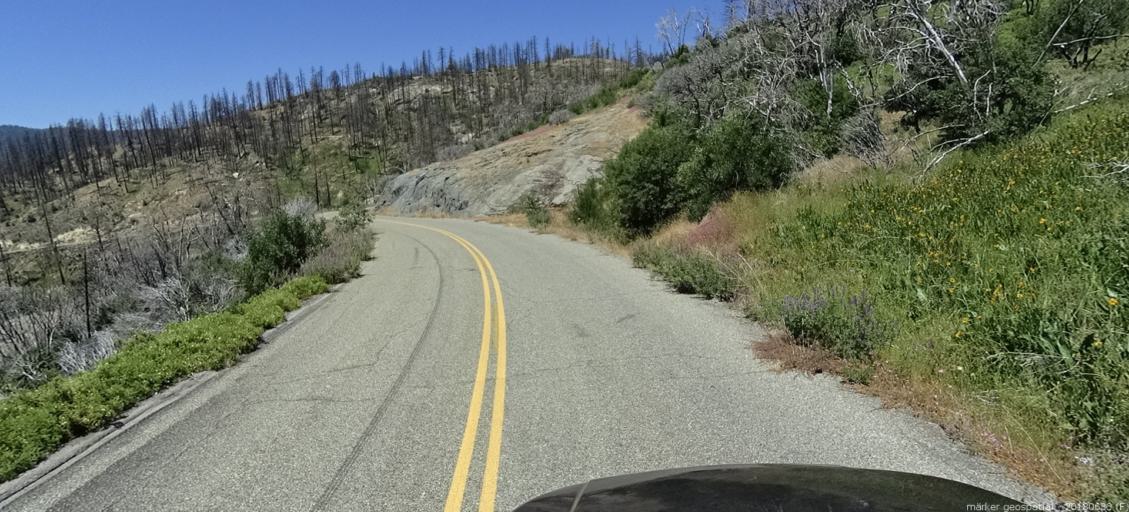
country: US
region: California
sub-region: Fresno County
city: Auberry
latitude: 37.3098
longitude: -119.3511
